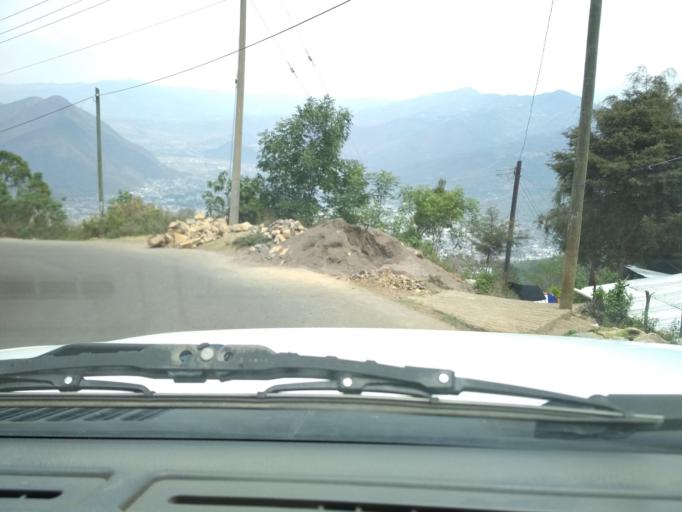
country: MX
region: Veracruz
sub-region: Camerino Z. Mendoza
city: La Cuesta
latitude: 18.7886
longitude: -97.1646
